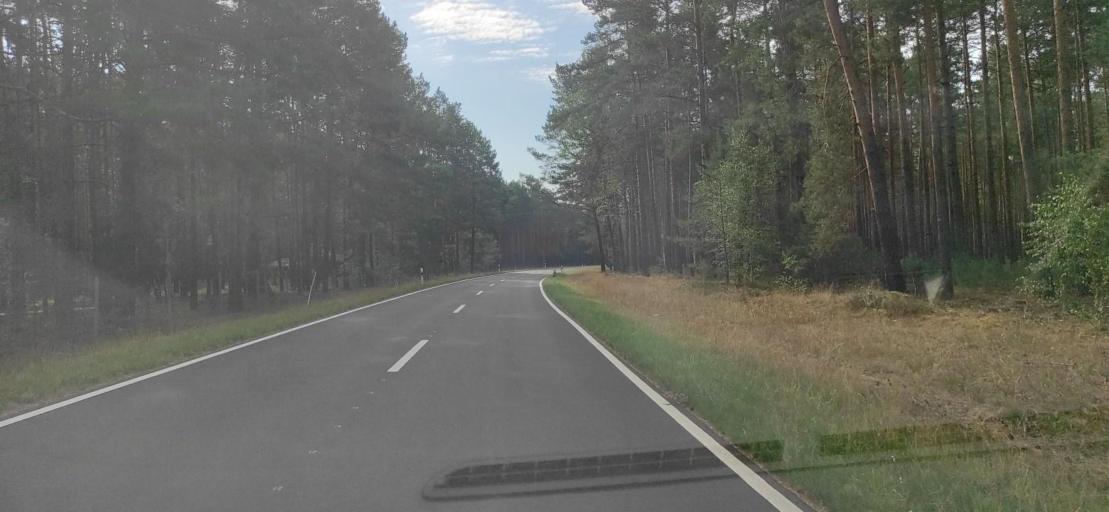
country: PL
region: Lubusz
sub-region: Powiat zarski
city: Trzebiel
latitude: 51.6619
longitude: 14.7408
